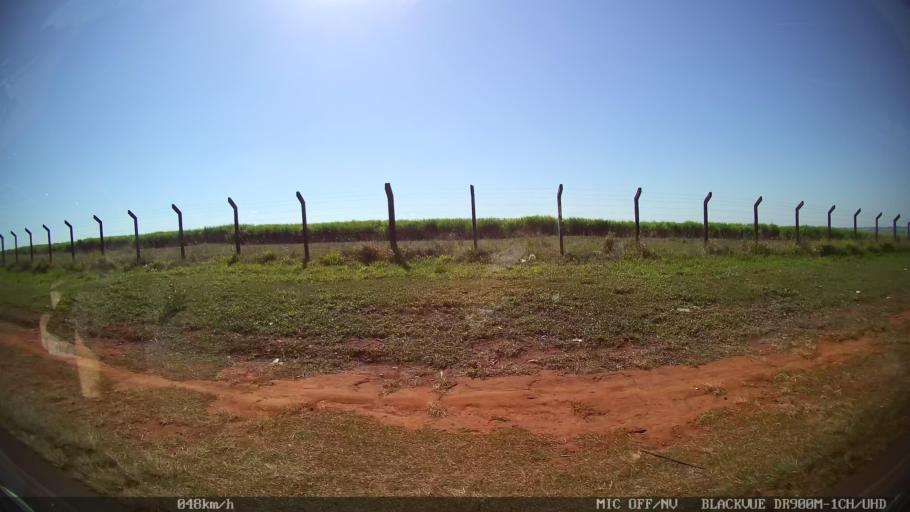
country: BR
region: Sao Paulo
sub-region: Batatais
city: Batatais
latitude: -20.8781
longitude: -47.5768
